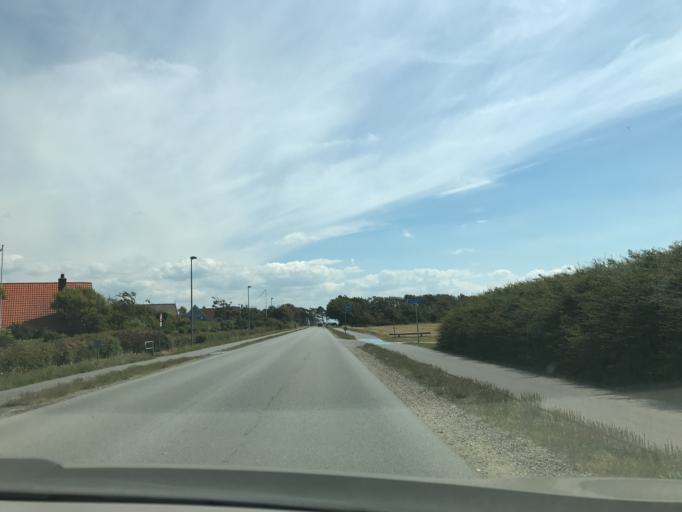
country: DK
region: Central Jutland
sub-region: Ringkobing-Skjern Kommune
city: Ringkobing
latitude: 56.0755
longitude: 8.2696
